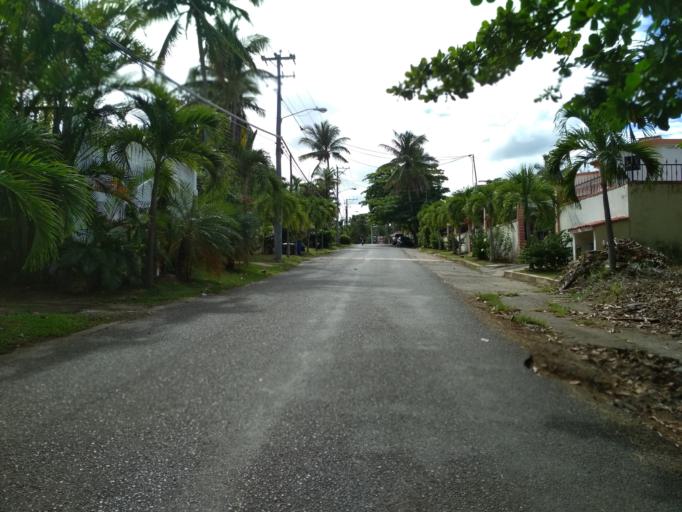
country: DO
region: Puerto Plata
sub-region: Puerto Plata
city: Puerto Plata
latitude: 19.8092
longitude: -70.7120
